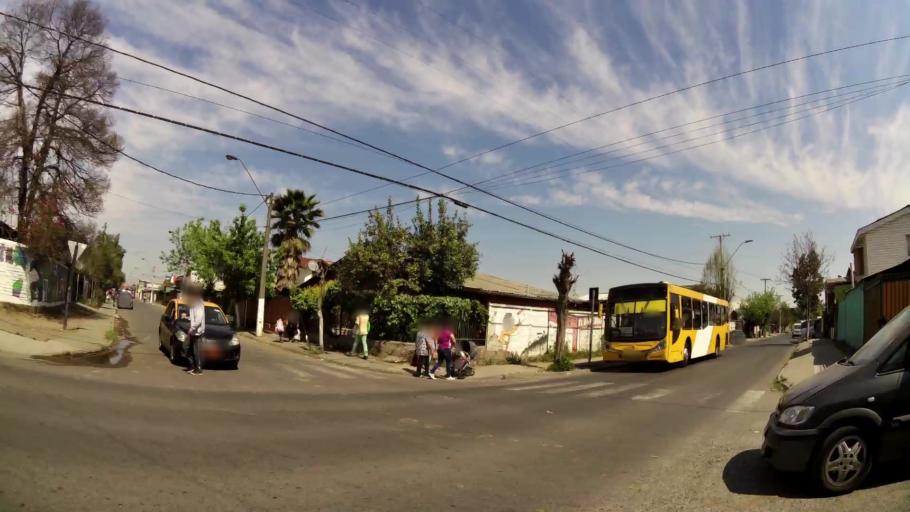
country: CL
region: Santiago Metropolitan
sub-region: Provincia de Santiago
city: La Pintana
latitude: -33.5529
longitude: -70.6416
